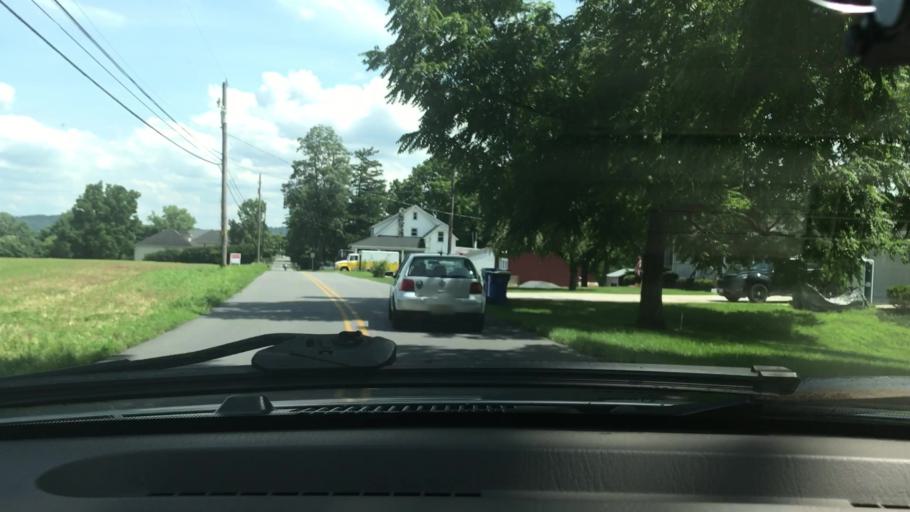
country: US
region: Pennsylvania
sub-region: Dauphin County
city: Rutherford
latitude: 40.2552
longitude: -76.7464
